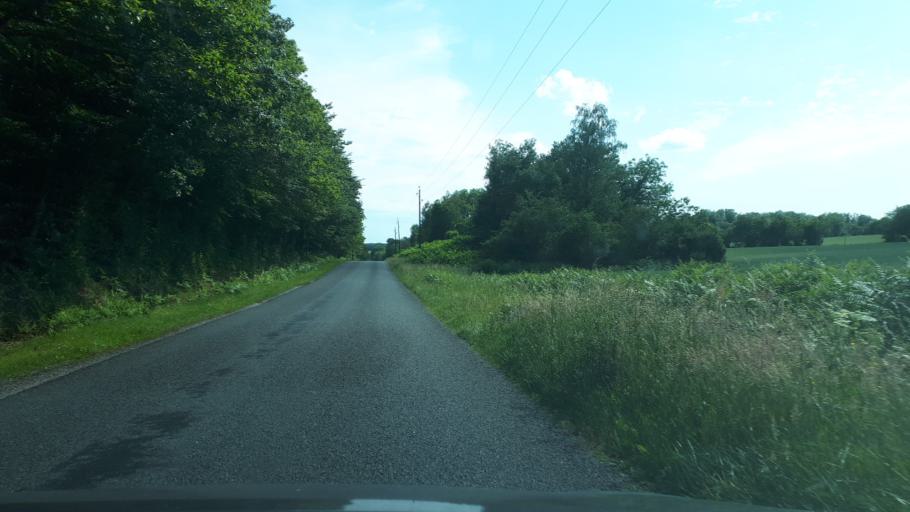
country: FR
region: Centre
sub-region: Departement du Cher
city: Henrichemont
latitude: 47.3798
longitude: 2.5967
